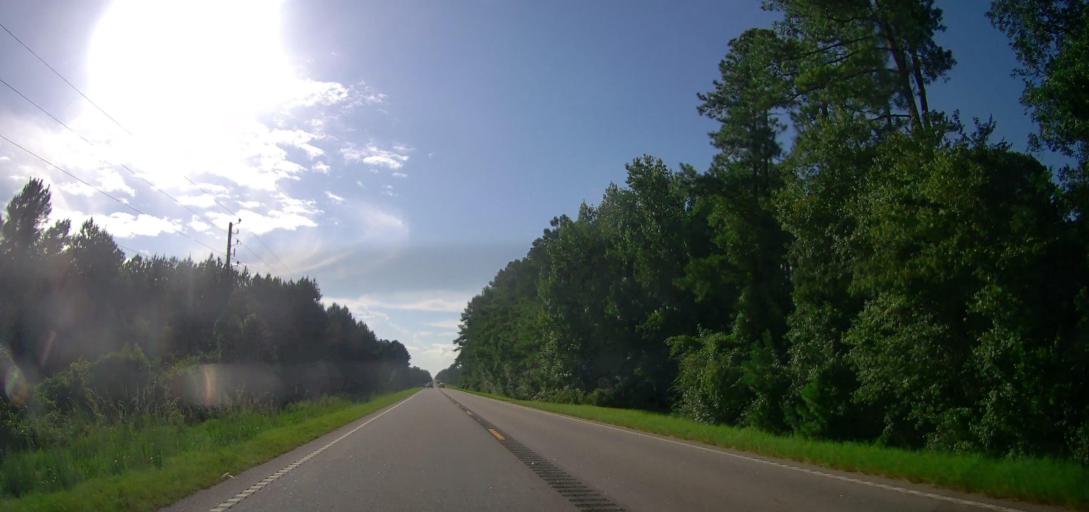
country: US
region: Georgia
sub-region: Coffee County
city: Douglas
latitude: 31.4657
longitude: -82.7597
